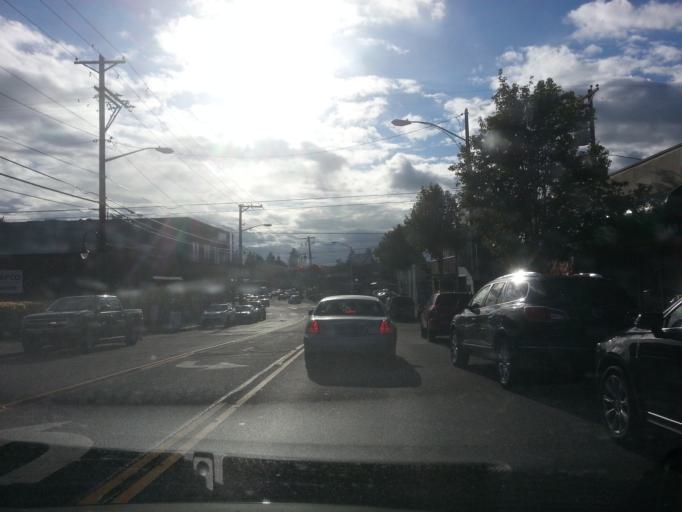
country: US
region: Washington
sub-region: Pierce County
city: Tacoma
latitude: 47.2555
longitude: -122.4726
